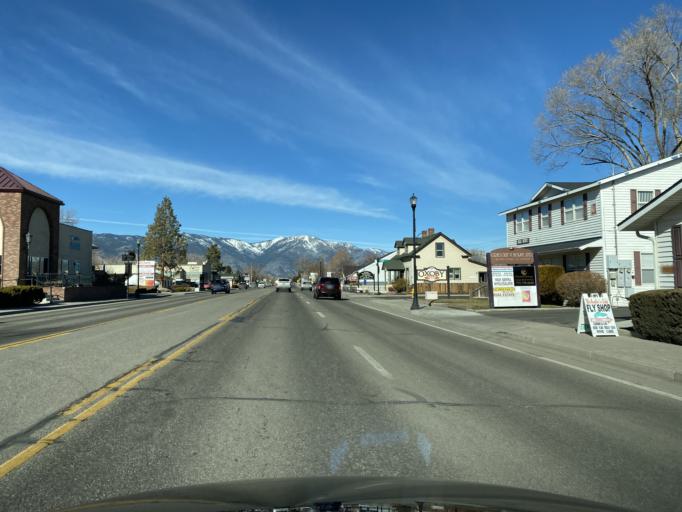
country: US
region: Nevada
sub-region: Douglas County
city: Gardnerville
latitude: 38.9449
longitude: -119.7535
